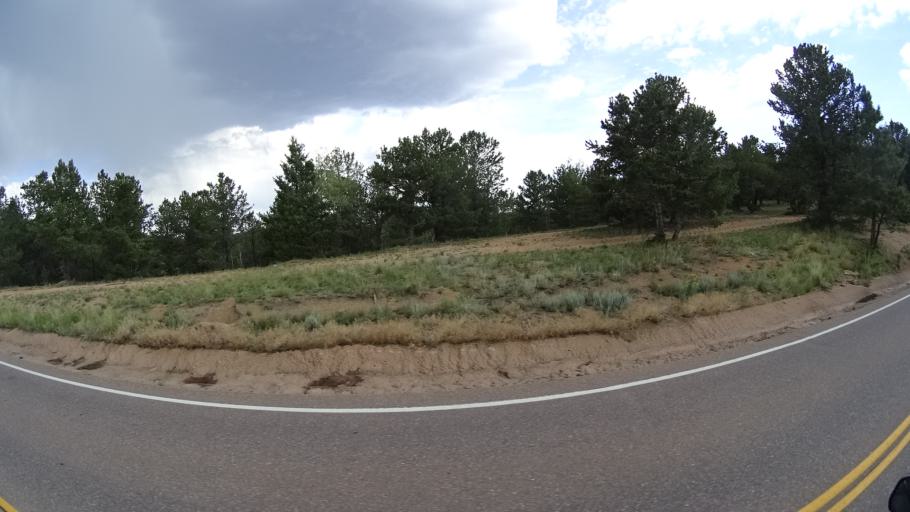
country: US
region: Colorado
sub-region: El Paso County
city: Cascade-Chipita Park
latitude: 38.9049
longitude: -105.0583
